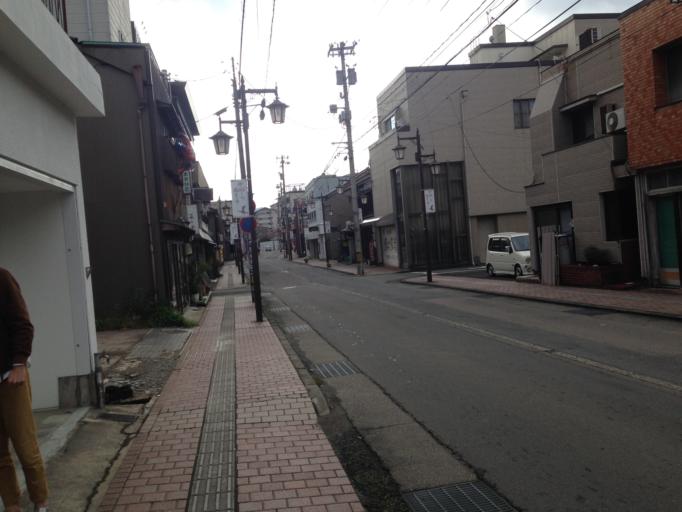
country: JP
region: Ishikawa
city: Komatsu
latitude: 36.2917
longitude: 136.3630
